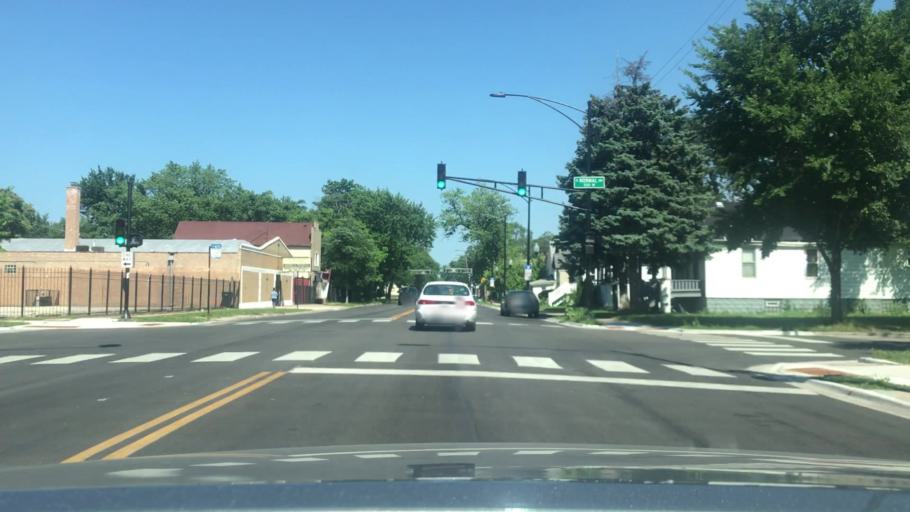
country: US
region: Illinois
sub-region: Cook County
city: Calumet Park
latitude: 41.7070
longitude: -87.6358
